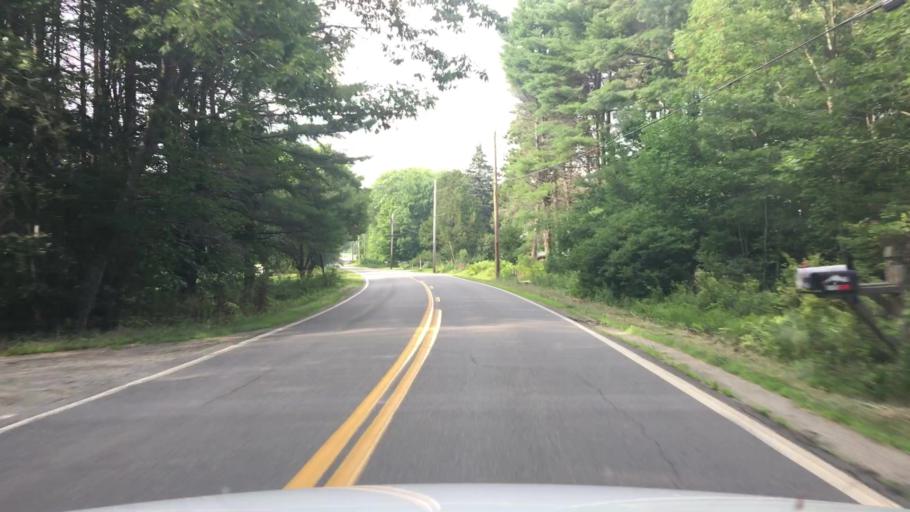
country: US
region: Maine
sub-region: Lincoln County
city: Waldoboro
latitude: 44.1639
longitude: -69.3776
